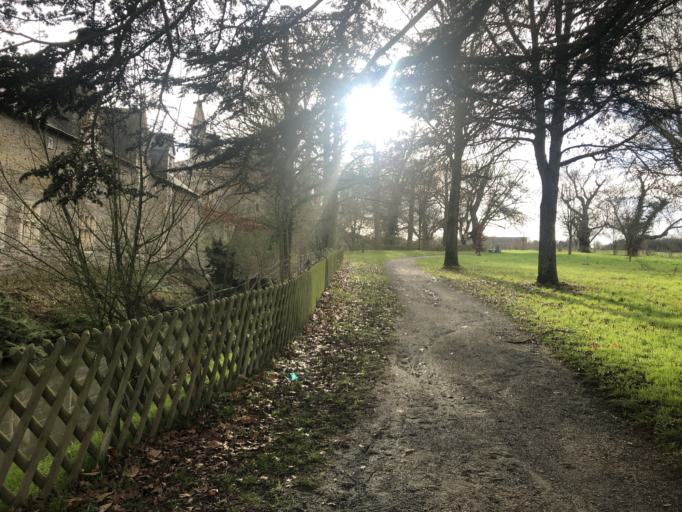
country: FR
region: Pays de la Loire
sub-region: Departement de Maine-et-Loire
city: Le Plessis-Mace
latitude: 47.5454
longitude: -0.6761
